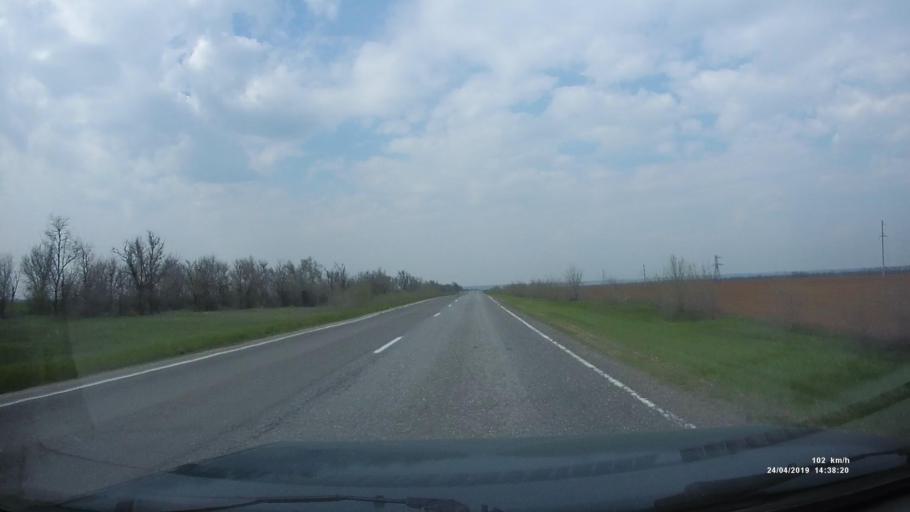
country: RU
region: Rostov
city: Remontnoye
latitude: 46.3991
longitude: 43.8861
